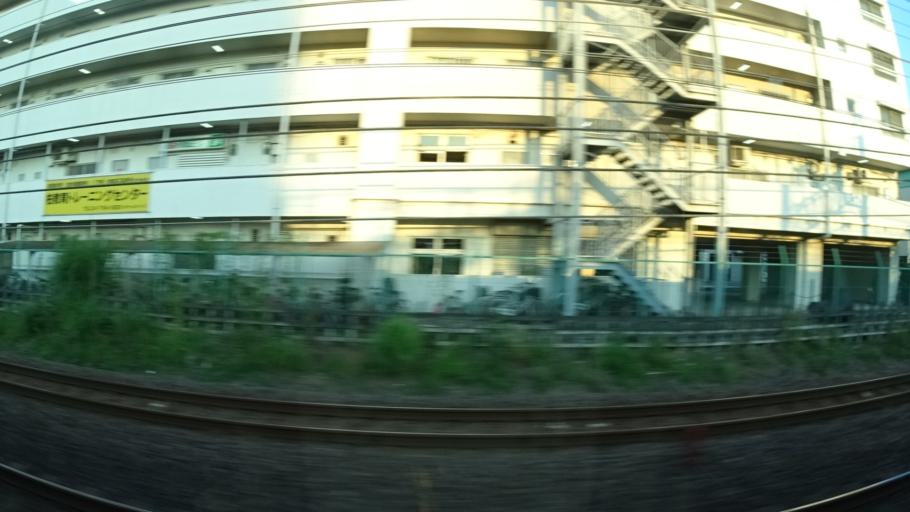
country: JP
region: Chiba
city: Kashiwa
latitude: 35.8597
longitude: 139.9688
